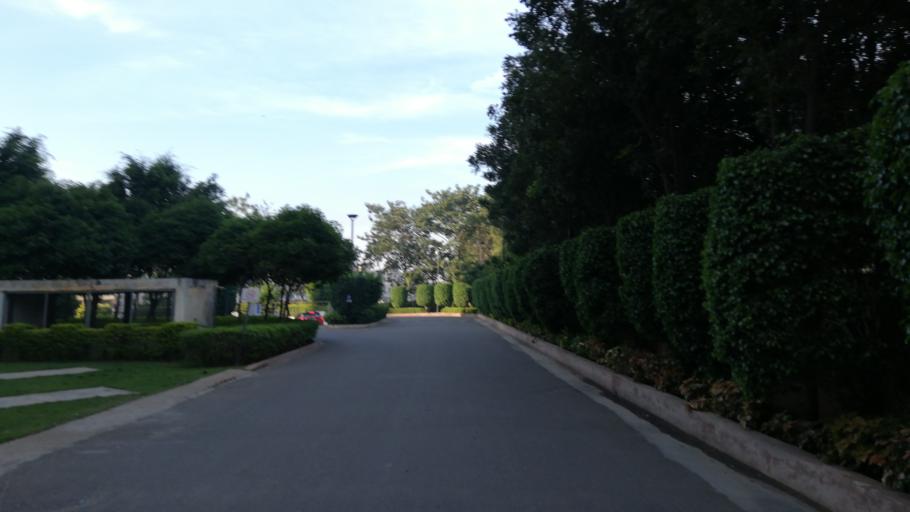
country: IN
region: Telangana
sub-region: Rangareddi
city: Kukatpalli
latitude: 17.4105
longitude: 78.3747
